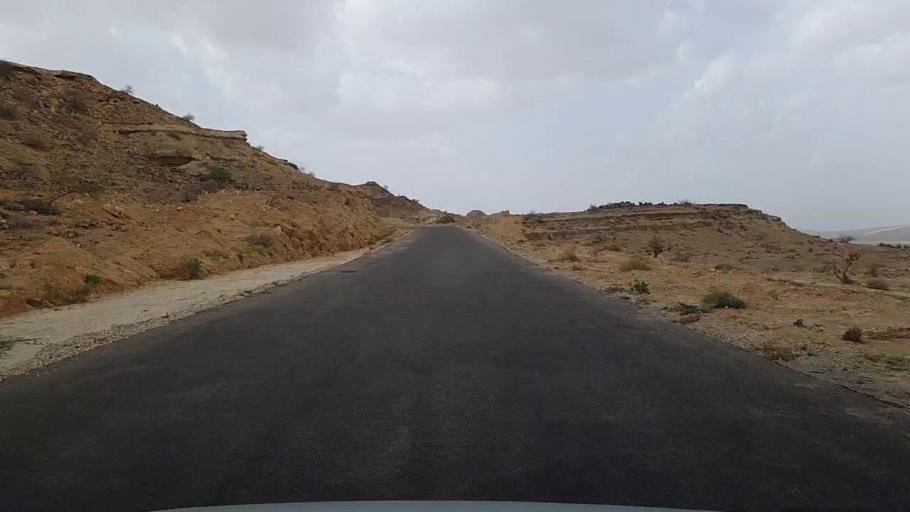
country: PK
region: Sindh
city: Jamshoro
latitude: 25.4239
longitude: 67.6910
